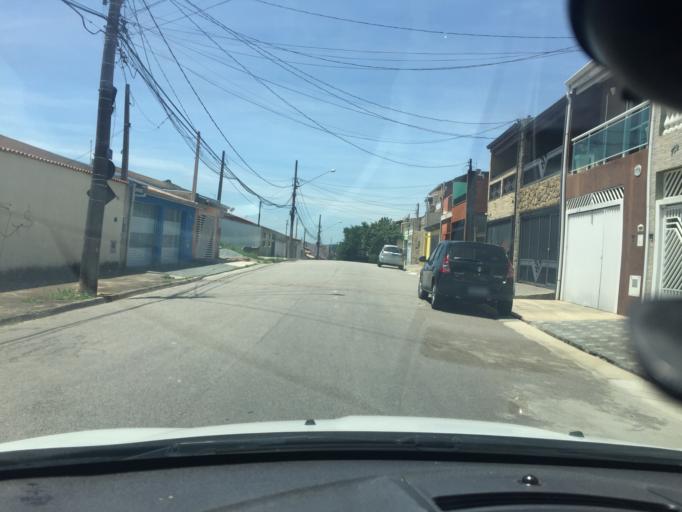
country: BR
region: Sao Paulo
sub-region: Jundiai
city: Jundiai
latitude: -23.2297
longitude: -46.8839
